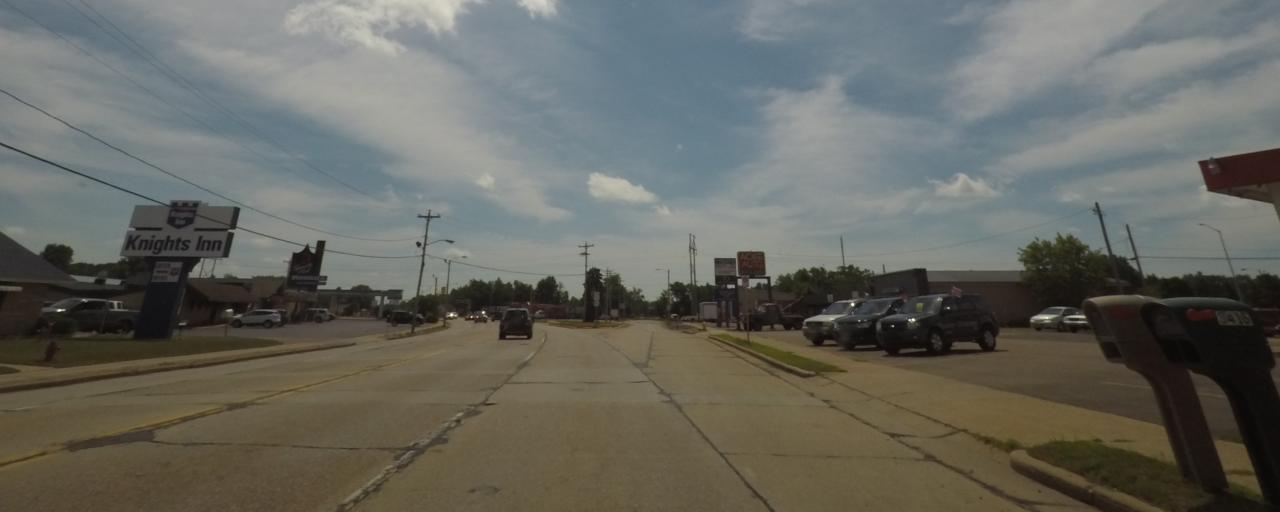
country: US
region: Wisconsin
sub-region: Portage County
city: Whiting
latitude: 44.4993
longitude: -89.5629
